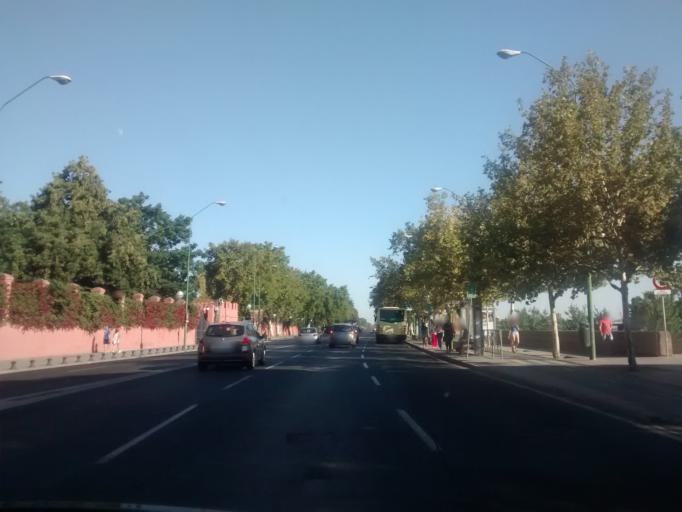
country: ES
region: Andalusia
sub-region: Provincia de Sevilla
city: Sevilla
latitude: 37.3797
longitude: -5.9942
